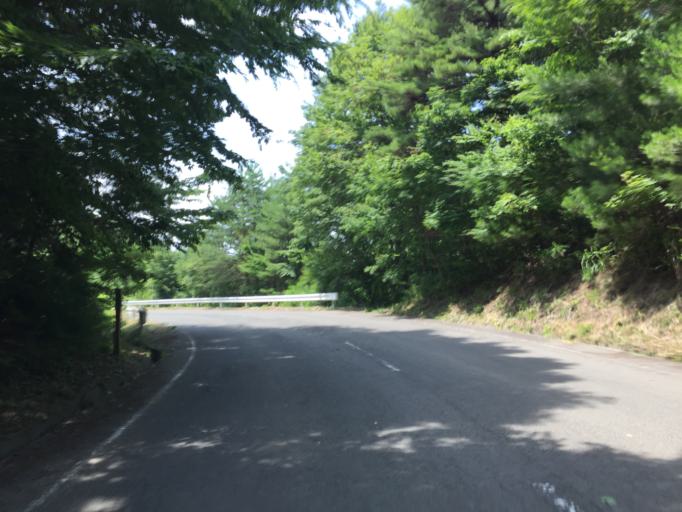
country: JP
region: Fukushima
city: Hobaramachi
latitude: 37.6708
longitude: 140.6550
